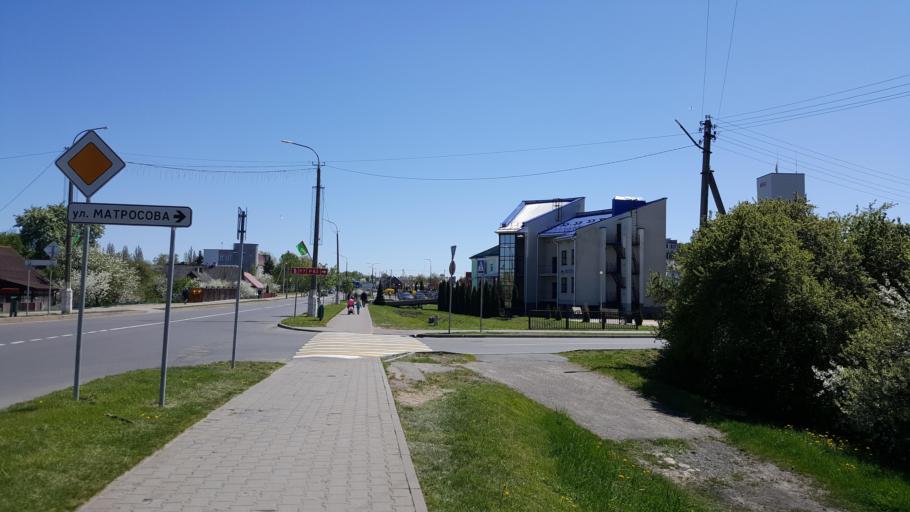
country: BY
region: Brest
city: Kamyanyets
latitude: 52.3992
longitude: 23.8241
